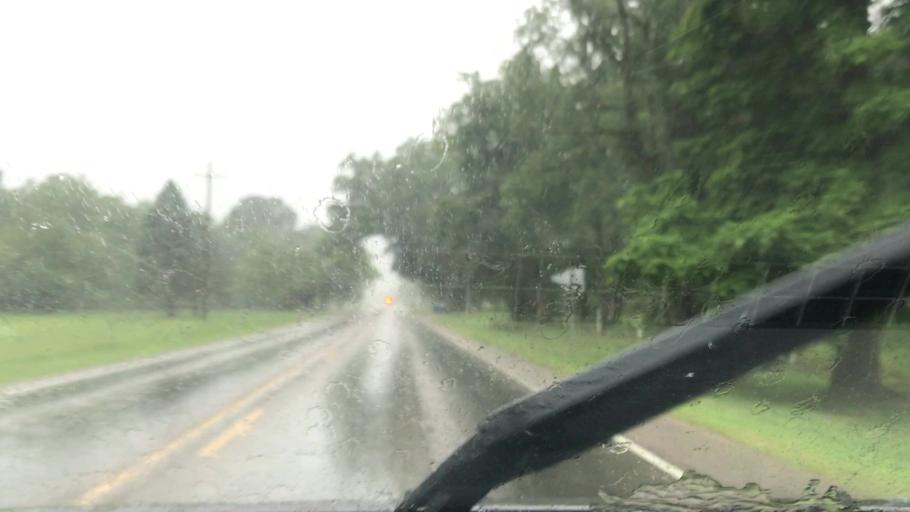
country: US
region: Indiana
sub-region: Hamilton County
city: Sheridan
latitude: 40.1246
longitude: -86.1979
